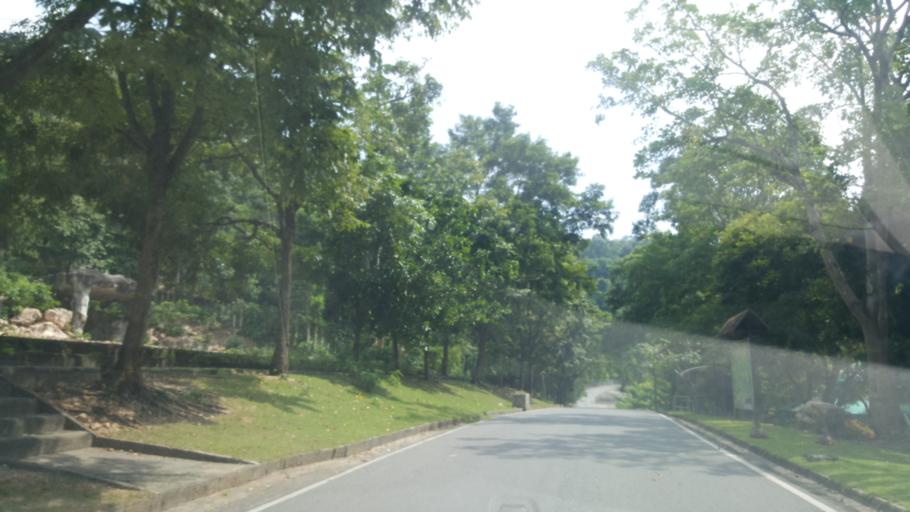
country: TH
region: Chon Buri
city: Ban Bueng
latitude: 13.2146
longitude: 101.0632
